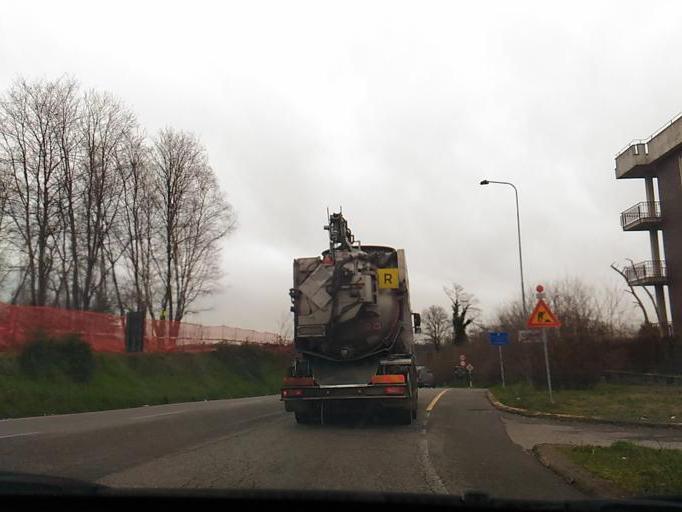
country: IT
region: Lombardy
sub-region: Provincia di Como
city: Carimate
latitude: 45.6920
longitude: 9.1062
